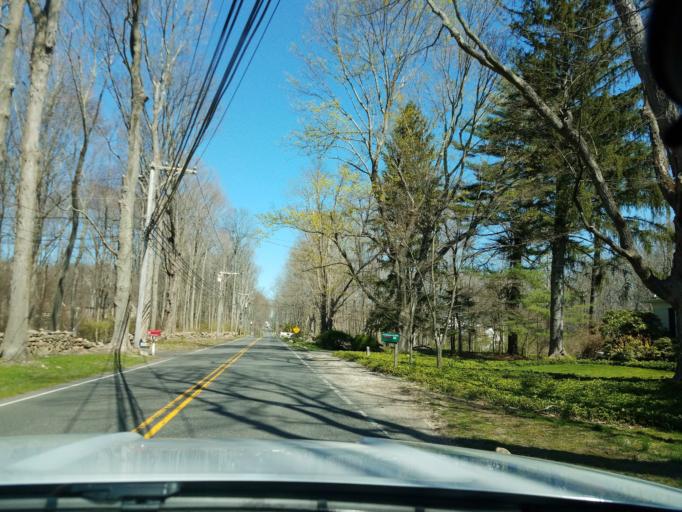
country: US
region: Connecticut
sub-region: Fairfield County
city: Westport
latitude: 41.2079
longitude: -73.3712
